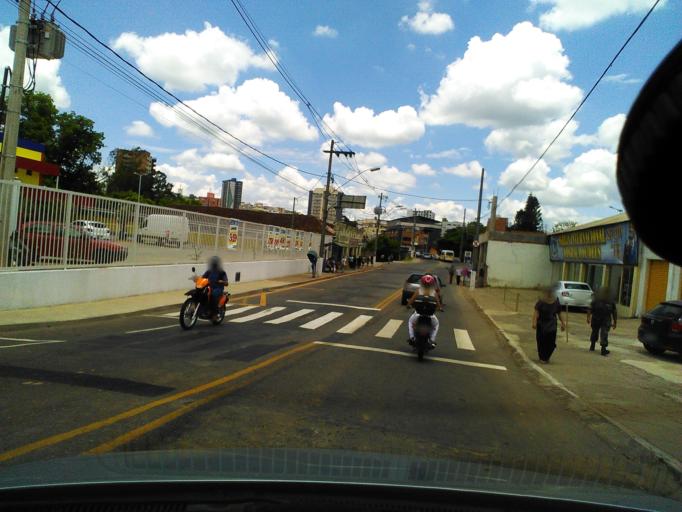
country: BR
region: Minas Gerais
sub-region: Tres Coracoes
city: Tres Coracoes
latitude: -21.6999
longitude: -45.2606
